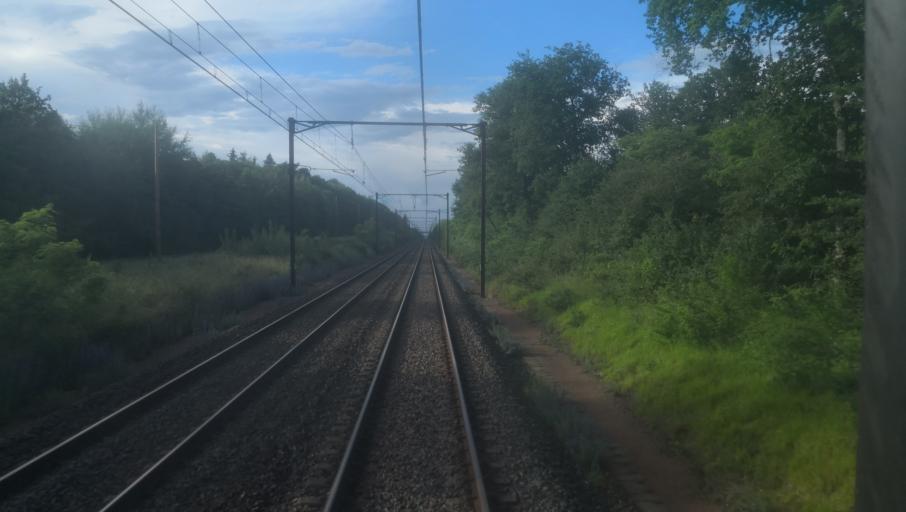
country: FR
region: Centre
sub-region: Departement du Loir-et-Cher
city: Nouan-le-Fuzelier
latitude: 47.4958
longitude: 2.0374
